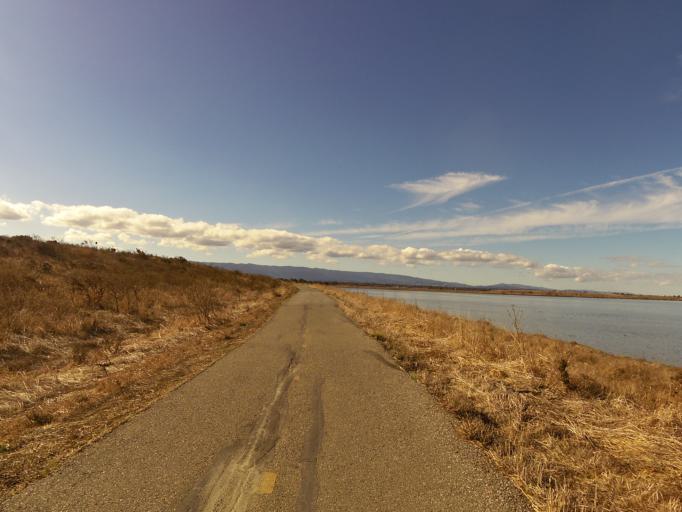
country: US
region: California
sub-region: Santa Clara County
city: Mountain View
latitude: 37.4359
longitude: -122.0734
